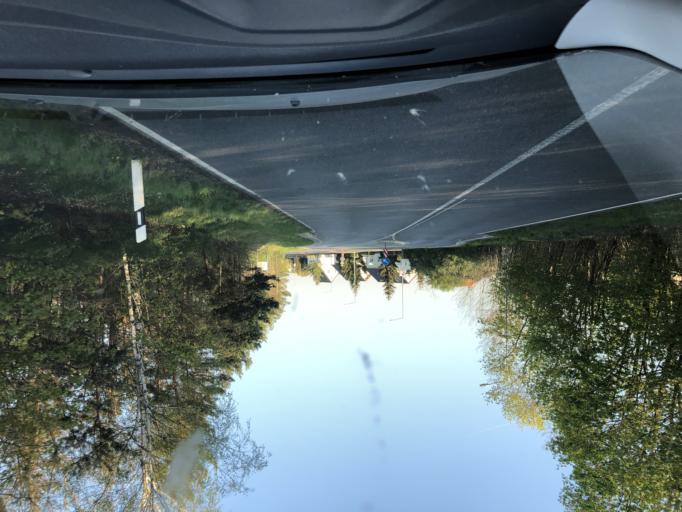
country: DE
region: Brandenburg
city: Ruhland
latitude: 51.4678
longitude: 13.8848
